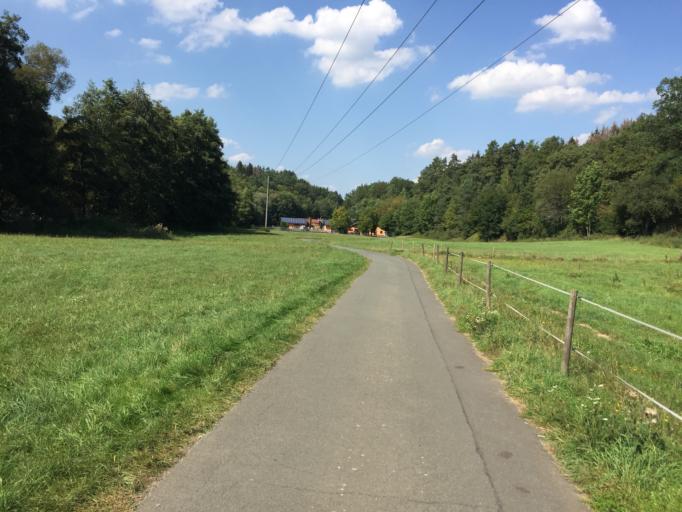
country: DE
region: Hesse
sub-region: Regierungsbezirk Giessen
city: Braunfels
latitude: 50.5045
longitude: 8.4206
